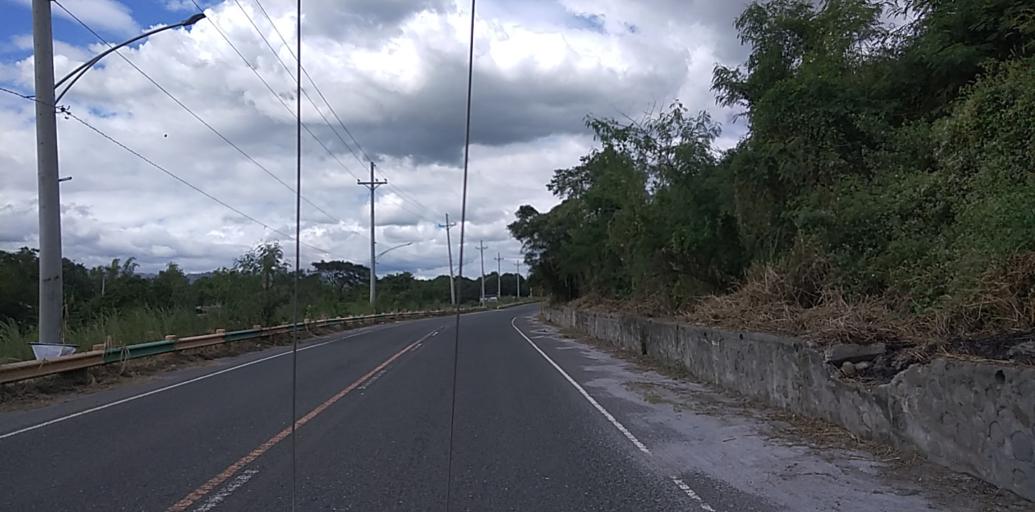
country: PH
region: Central Luzon
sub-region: Province of Pampanga
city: Dolores
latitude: 15.0989
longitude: 120.5254
